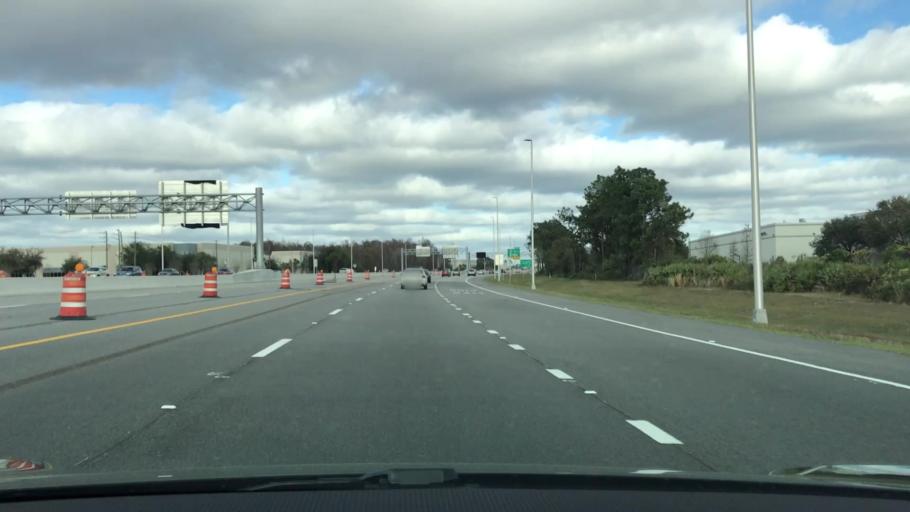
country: US
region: Florida
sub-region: Orange County
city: Williamsburg
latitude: 28.4278
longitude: -81.4163
